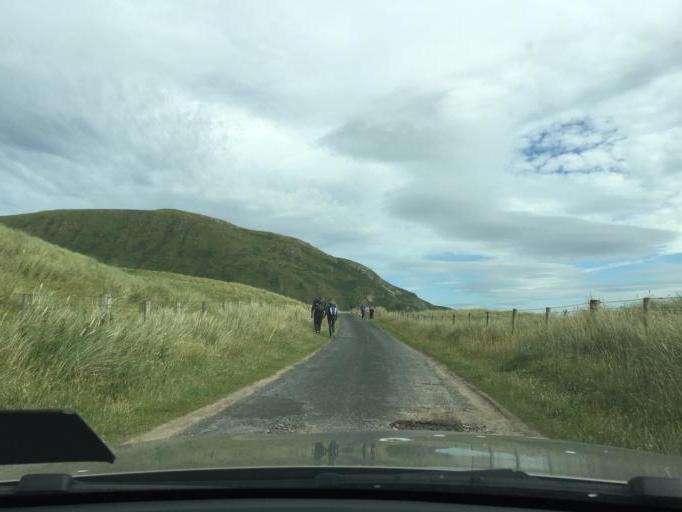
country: IE
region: Ulster
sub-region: County Donegal
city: Carndonagh
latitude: 55.3223
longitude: -7.3282
